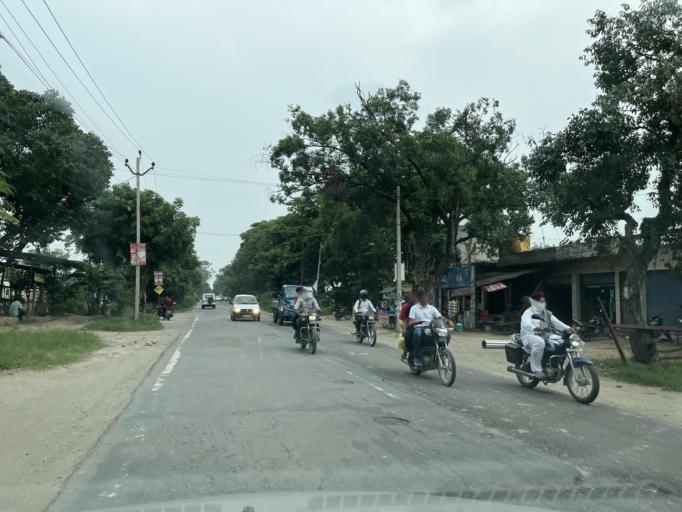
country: IN
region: Uttar Pradesh
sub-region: Rampur
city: Bilaspur
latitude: 29.0302
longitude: 79.2636
